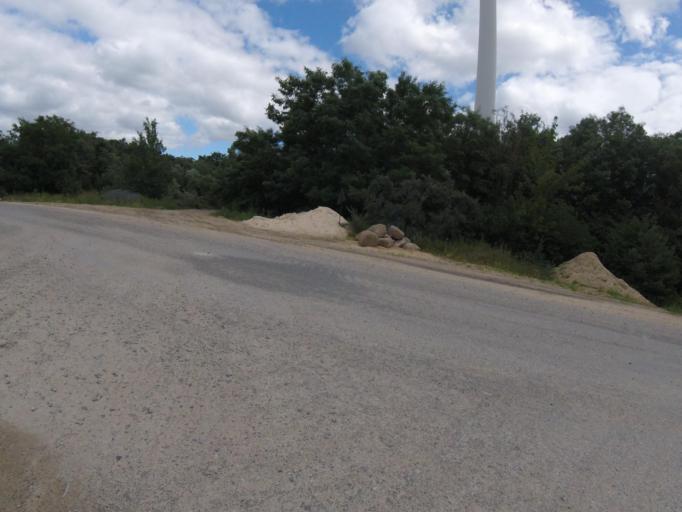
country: DE
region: Brandenburg
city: Wildau
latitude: 52.3259
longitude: 13.6779
